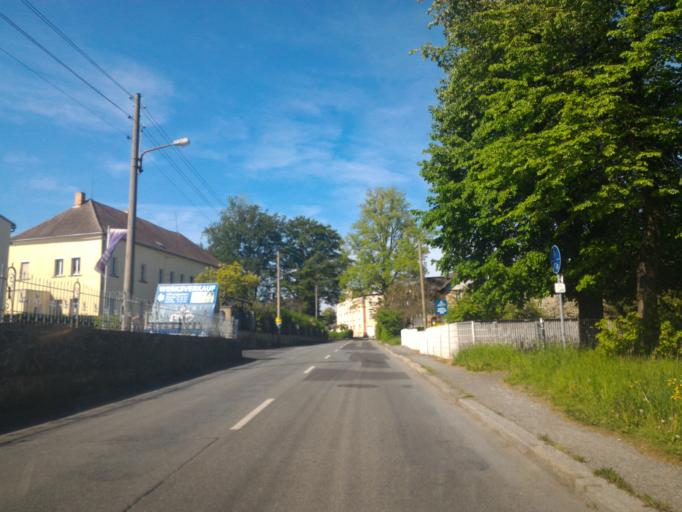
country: DE
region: Saxony
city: Eibau
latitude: 50.9785
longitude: 14.6649
